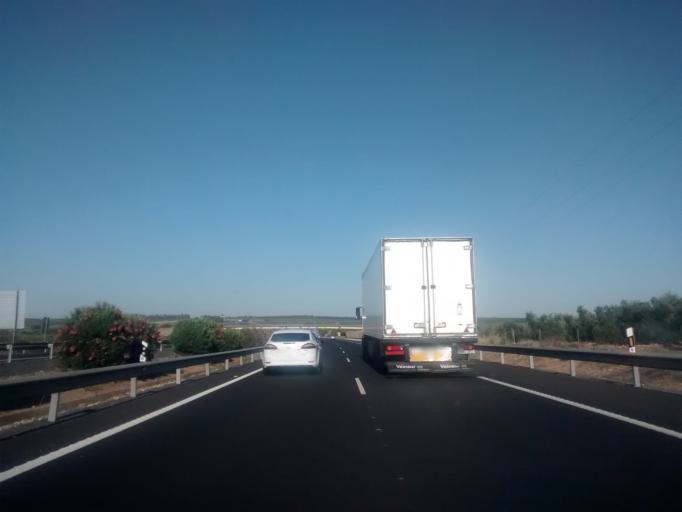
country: ES
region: Andalusia
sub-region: Provincia de Huelva
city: Chucena
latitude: 37.3531
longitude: -6.3984
